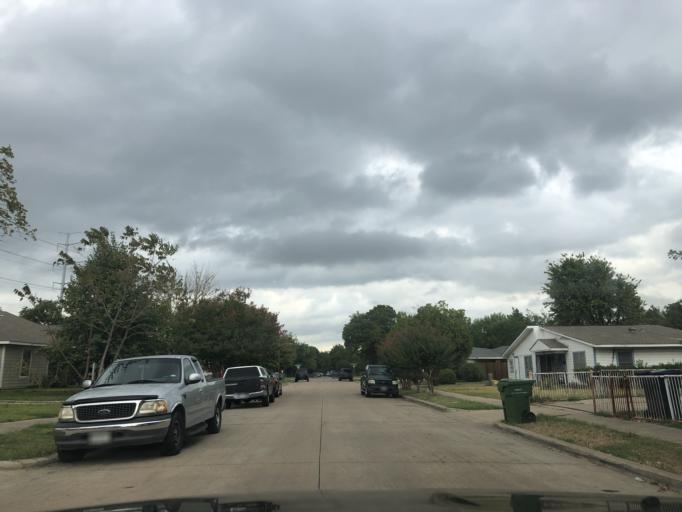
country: US
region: Texas
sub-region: Dallas County
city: Garland
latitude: 32.8897
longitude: -96.6512
